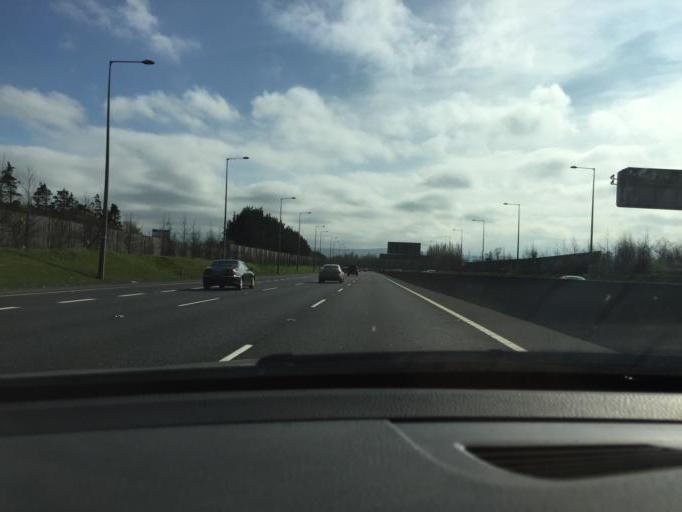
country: IE
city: Palmerstown
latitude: 53.3460
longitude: -6.3866
